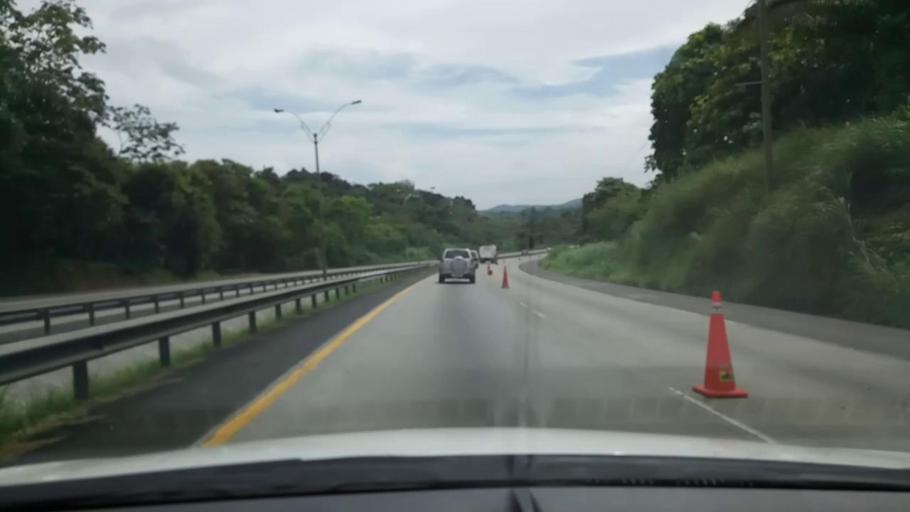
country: PA
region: Panama
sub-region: Distrito Arraijan
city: Arraijan
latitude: 8.9928
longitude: -79.6496
